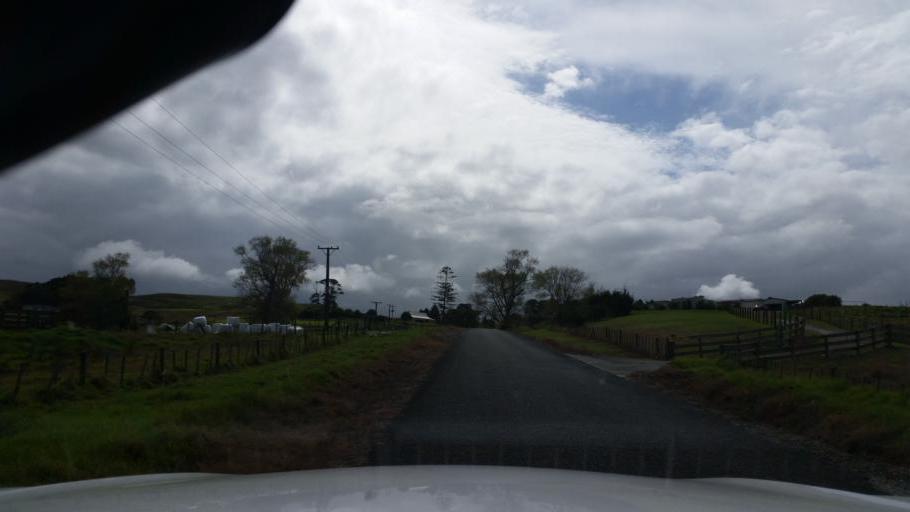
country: NZ
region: Northland
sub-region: Whangarei
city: Ruakaka
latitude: -36.1089
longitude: 174.2774
